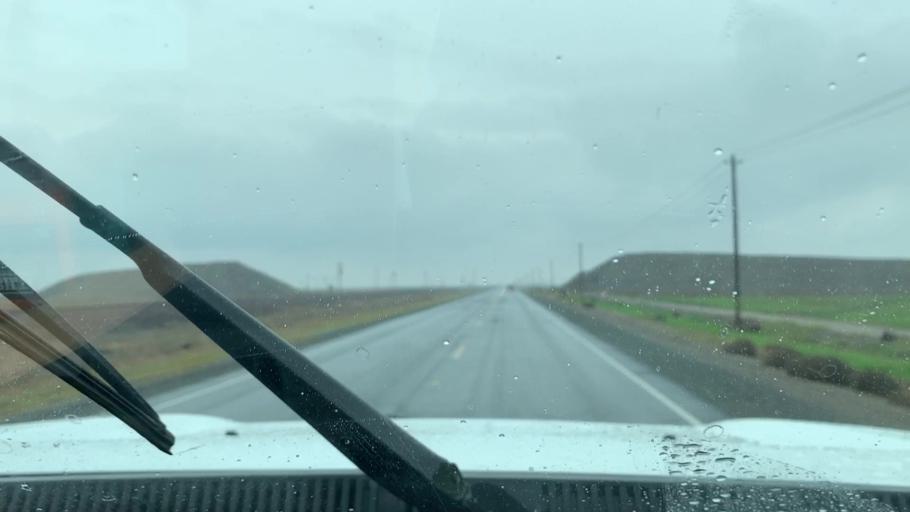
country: US
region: California
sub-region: Tulare County
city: Alpaugh
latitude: 35.9457
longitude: -119.4449
